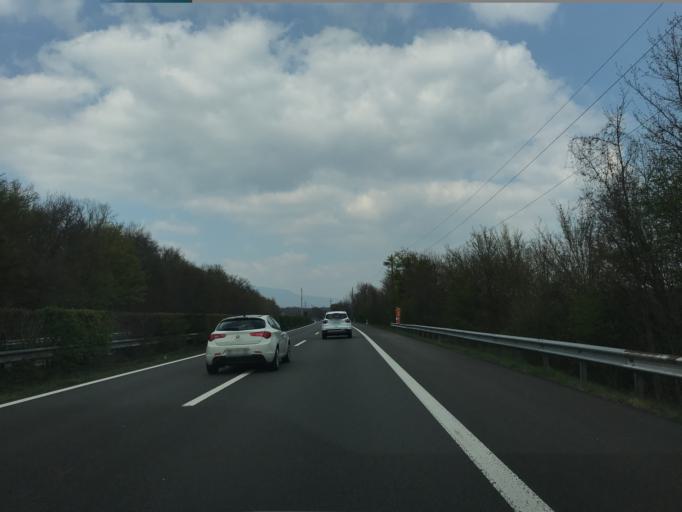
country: CH
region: Geneva
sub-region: Geneva
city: Versoix
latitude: 46.2898
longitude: 6.1462
